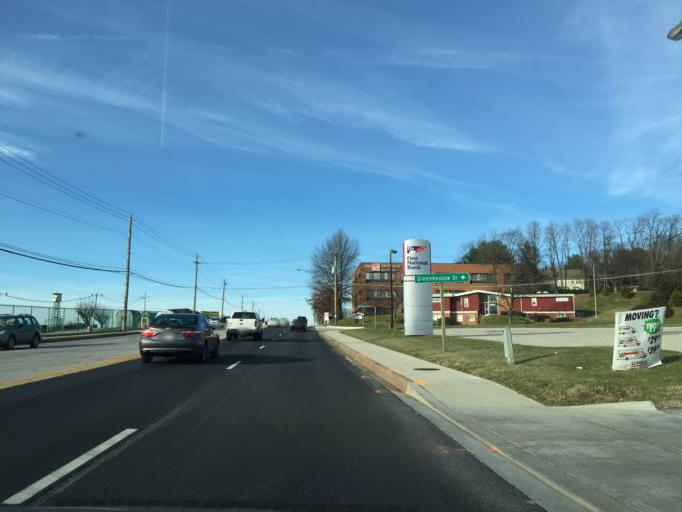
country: US
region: Maryland
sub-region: Baltimore County
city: Timonium
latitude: 39.4447
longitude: -76.6280
